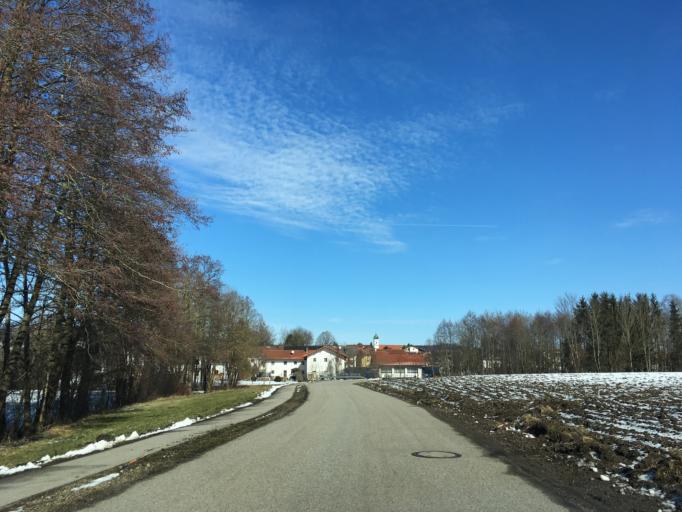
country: DE
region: Bavaria
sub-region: Upper Bavaria
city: Rechtmehring
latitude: 48.1143
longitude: 12.1504
